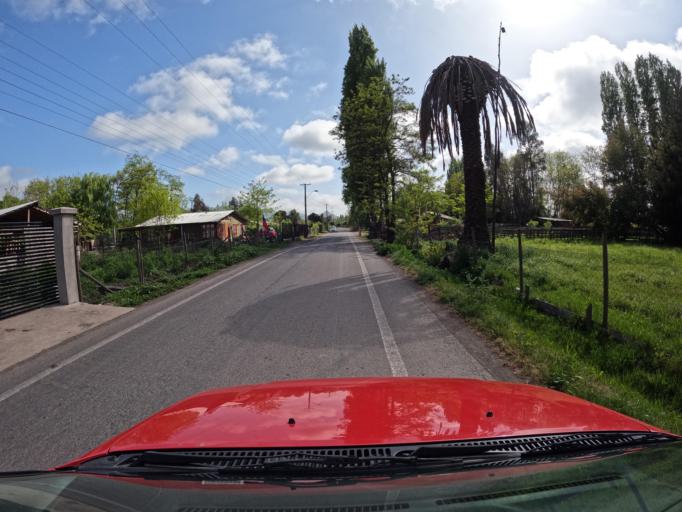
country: CL
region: Maule
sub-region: Provincia de Curico
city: Teno
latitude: -34.8831
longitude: -71.2265
